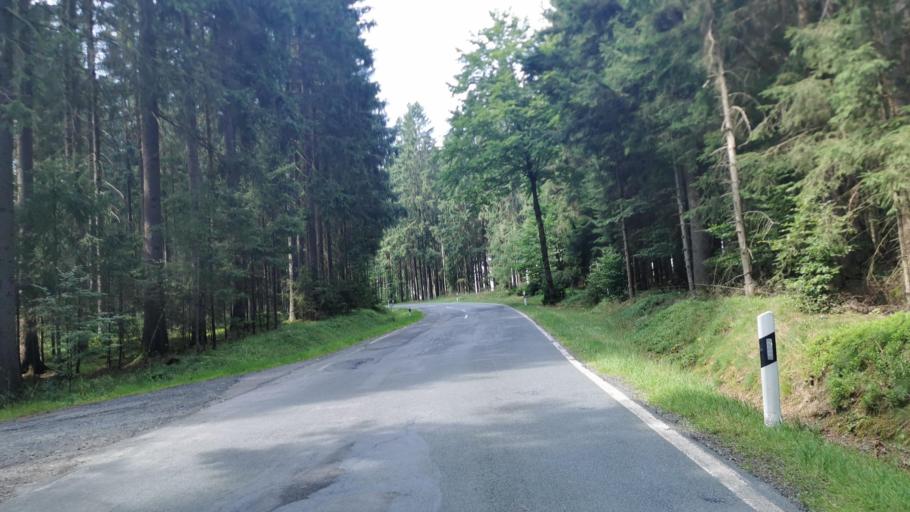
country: DE
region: Bavaria
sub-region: Upper Franconia
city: Tschirn
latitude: 50.3481
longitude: 11.4489
